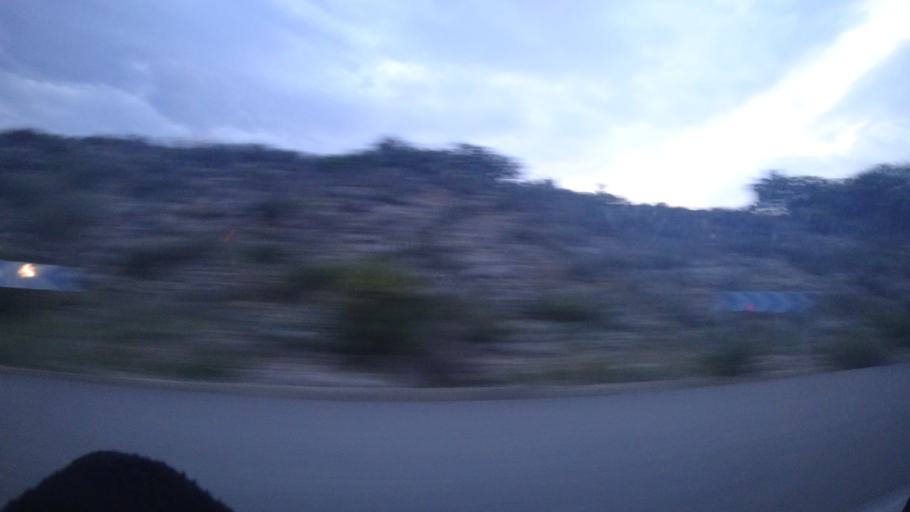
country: FR
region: Languedoc-Roussillon
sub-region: Departement de l'Aude
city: Leucate
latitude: 42.9395
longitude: 2.9682
